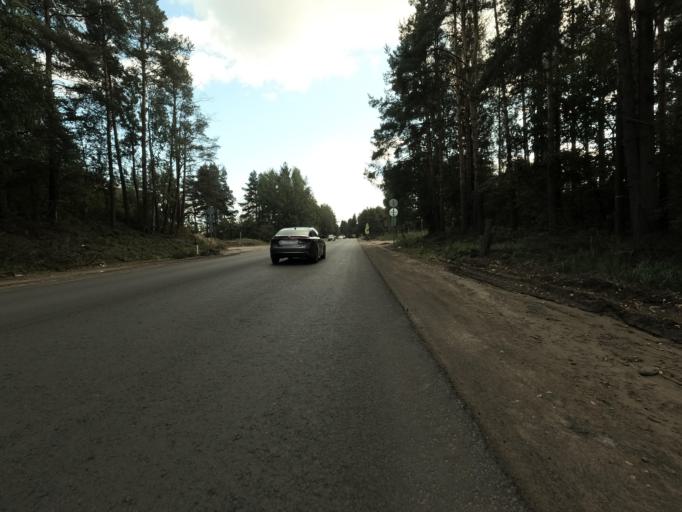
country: RU
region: Leningrad
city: Koltushi
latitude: 59.9637
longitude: 30.6584
